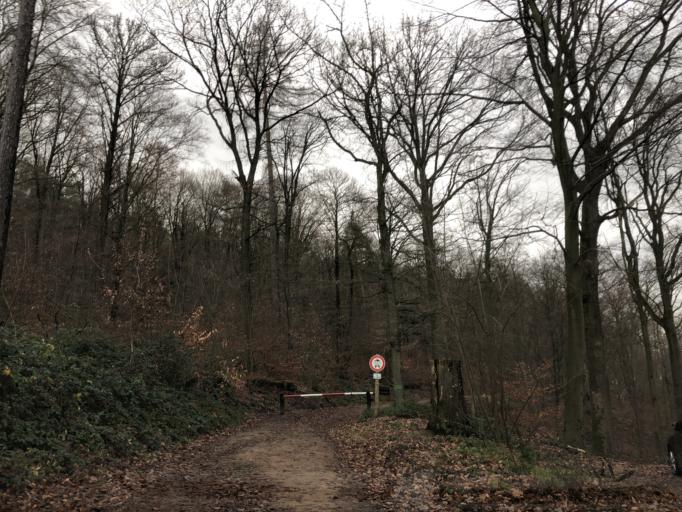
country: DE
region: Baden-Wuerttemberg
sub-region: Karlsruhe Region
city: Dossenheim
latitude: 49.4478
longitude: 8.6901
